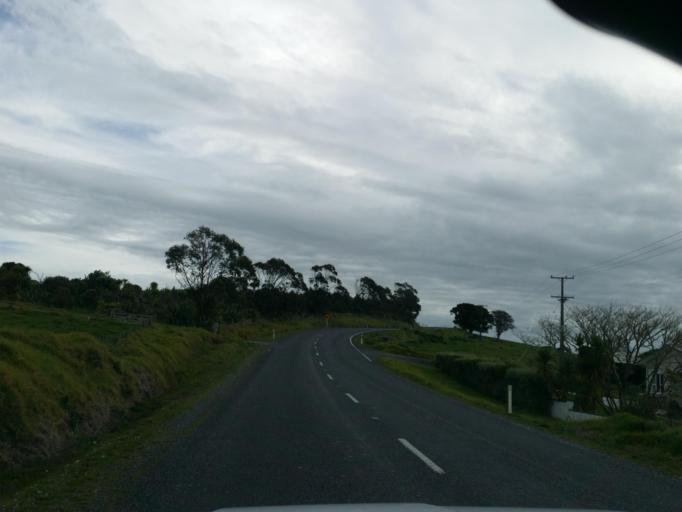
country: NZ
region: Northland
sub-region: Kaipara District
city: Dargaville
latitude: -35.9695
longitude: 173.9403
